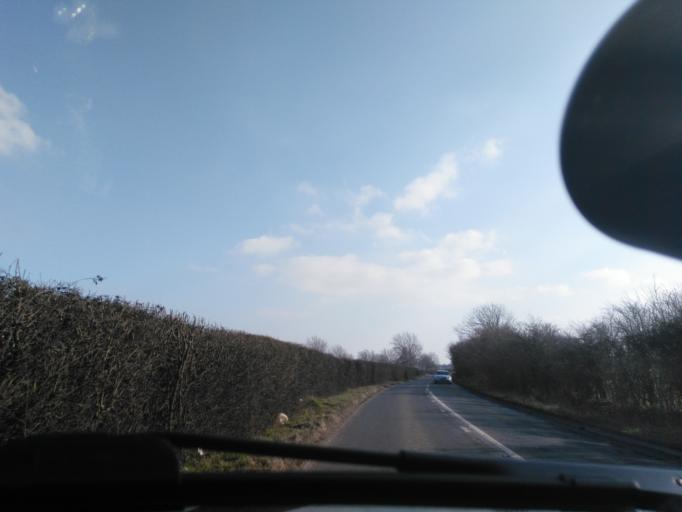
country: GB
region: England
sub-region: Wiltshire
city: Norton
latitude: 51.5347
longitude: -2.1296
